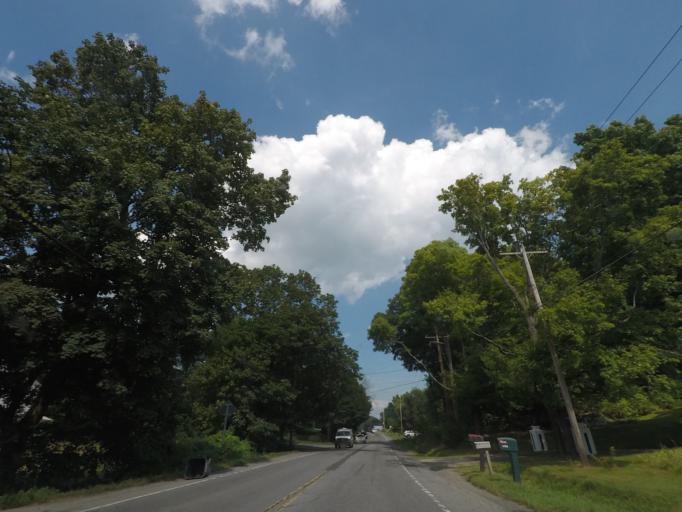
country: US
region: New York
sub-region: Saratoga County
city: Waterford
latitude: 42.7958
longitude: -73.6455
